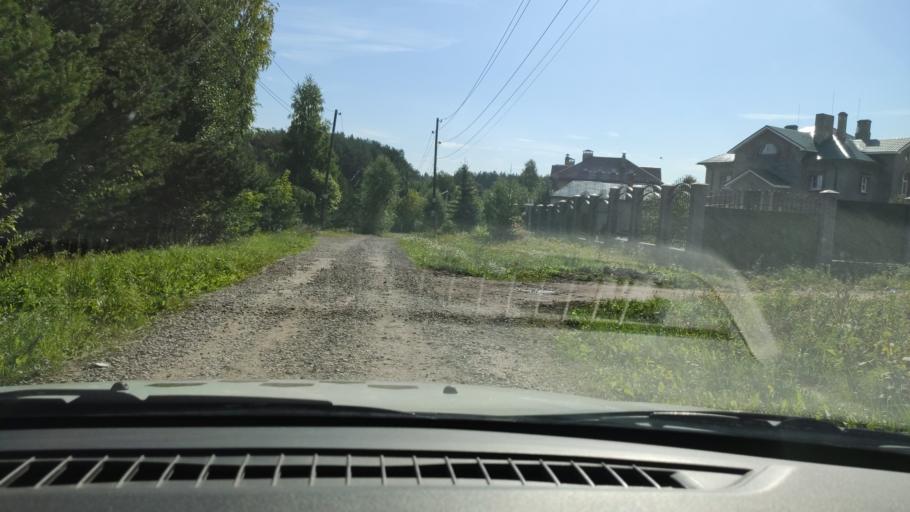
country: RU
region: Perm
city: Perm
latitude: 57.9861
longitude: 56.3068
